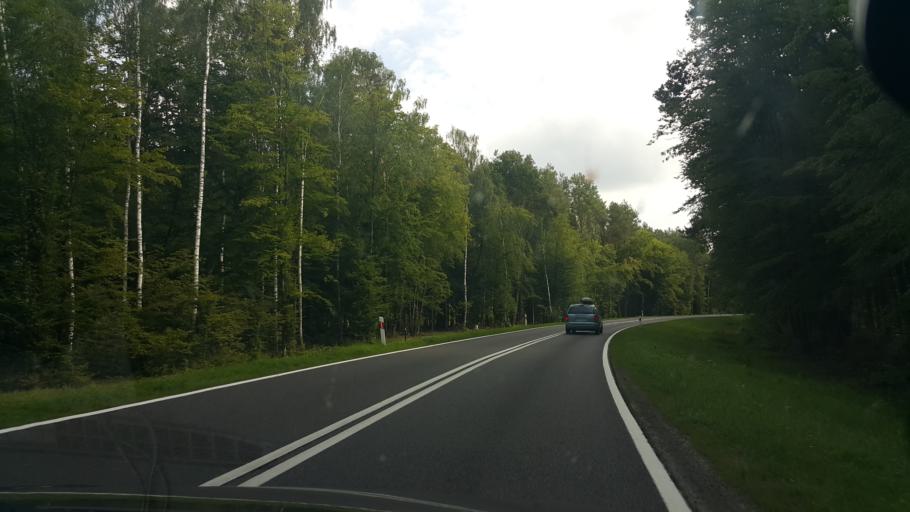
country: PL
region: Lublin Voivodeship
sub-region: Powiat wlodawski
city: Hansk
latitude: 51.5298
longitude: 23.4170
